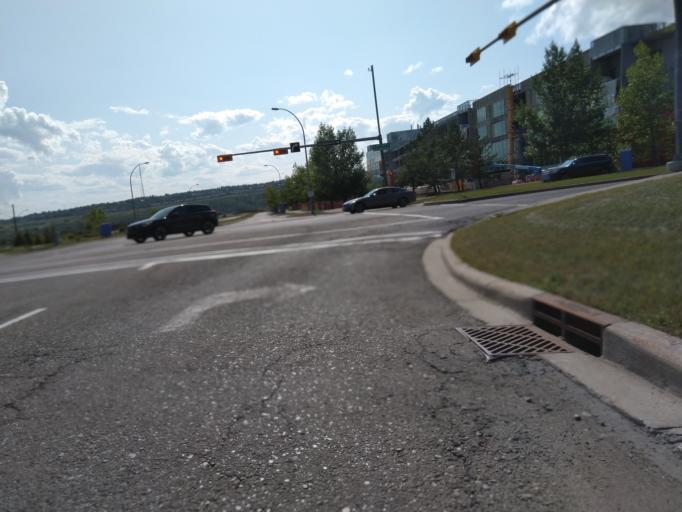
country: CA
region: Alberta
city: Calgary
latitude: 51.0742
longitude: -114.1441
